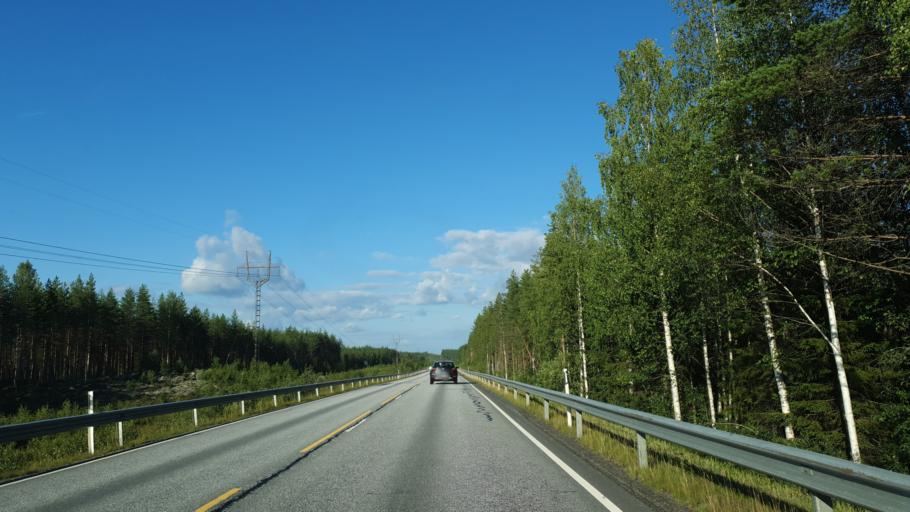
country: FI
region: North Karelia
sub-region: Joensuu
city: Outokumpu
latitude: 62.5289
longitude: 29.0785
